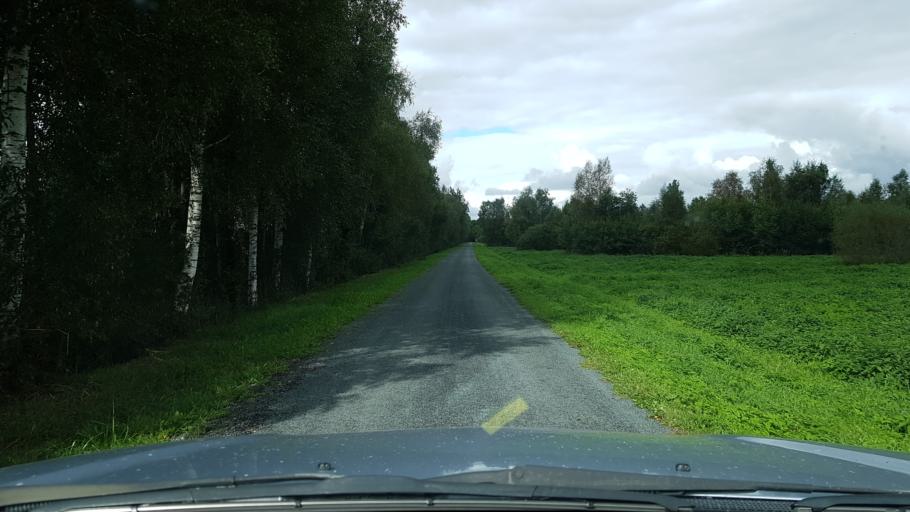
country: EE
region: Harju
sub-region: Raasiku vald
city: Arukula
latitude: 59.2836
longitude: 25.0717
